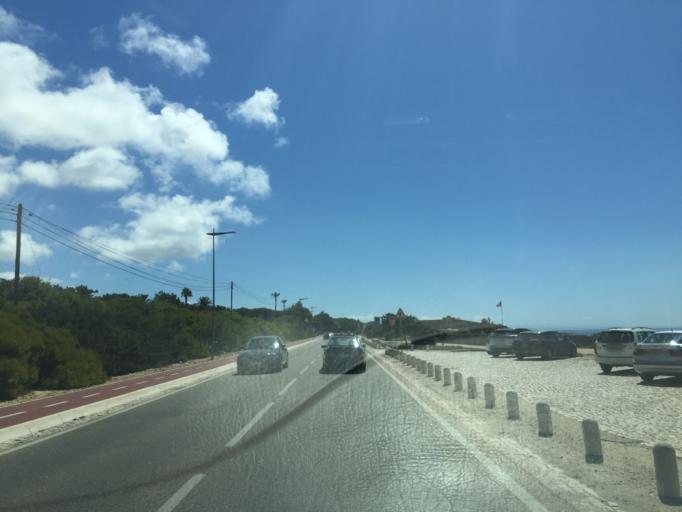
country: PT
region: Lisbon
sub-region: Cascais
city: Cascais
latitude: 38.7006
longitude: -9.4697
